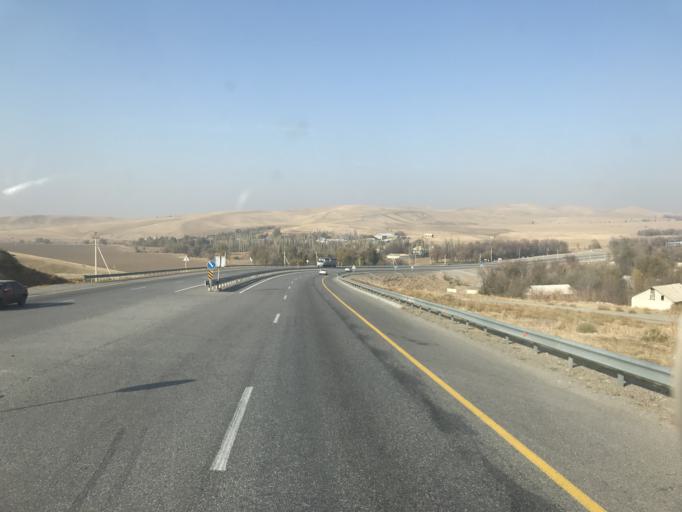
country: KZ
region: Ongtustik Qazaqstan
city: Sastobe
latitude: 42.4961
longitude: 69.9595
